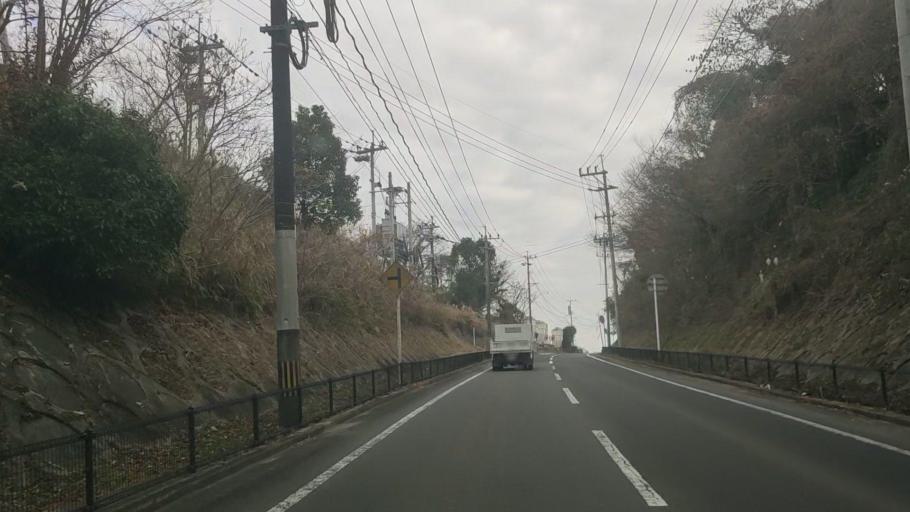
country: JP
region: Nagasaki
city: Shimabara
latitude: 32.8531
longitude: 130.2705
